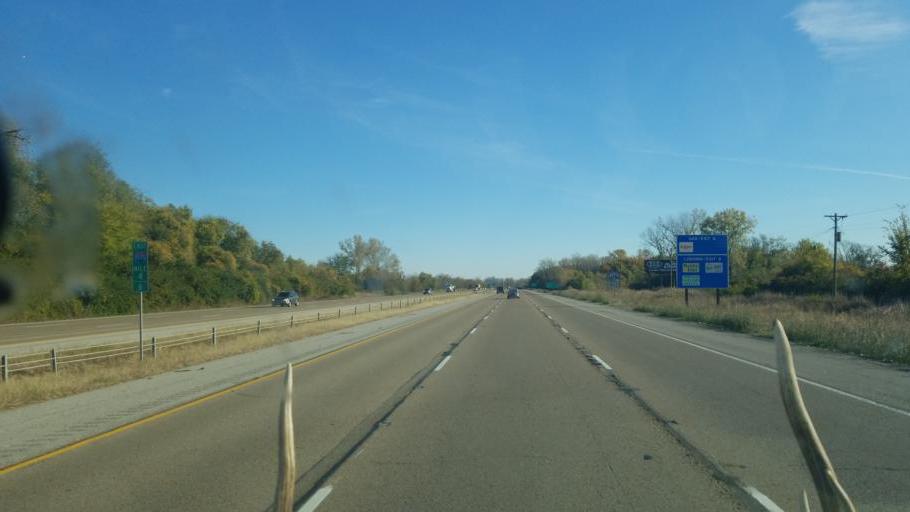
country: US
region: Illinois
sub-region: Saint Clair County
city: Fairmont City
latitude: 38.6505
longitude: -90.1207
